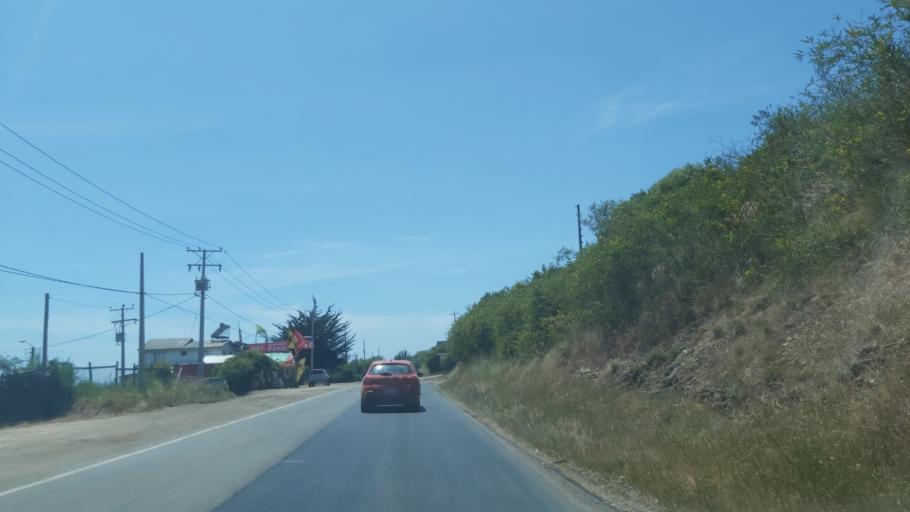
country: CL
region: Maule
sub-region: Provincia de Cauquenes
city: Cauquenes
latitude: -35.8257
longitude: -72.6063
